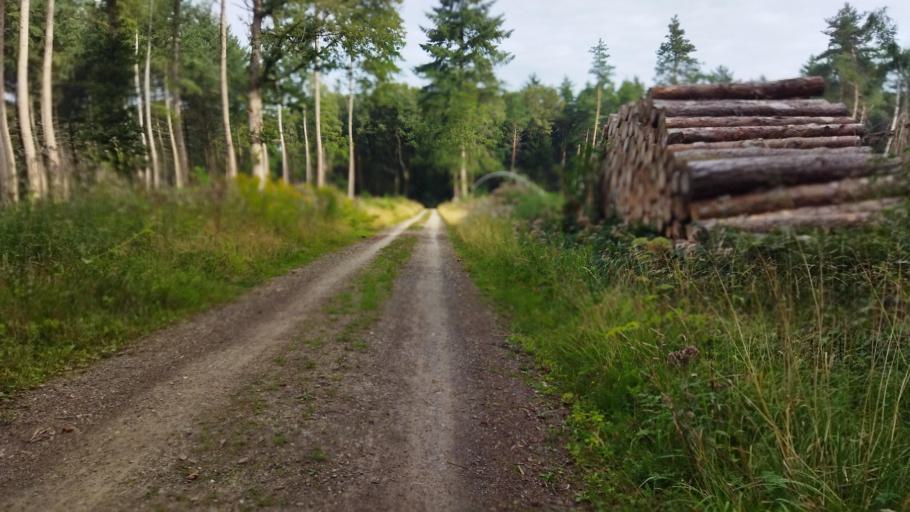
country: DE
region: Lower Saxony
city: Bad Rothenfelde
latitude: 52.0837
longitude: 8.1589
